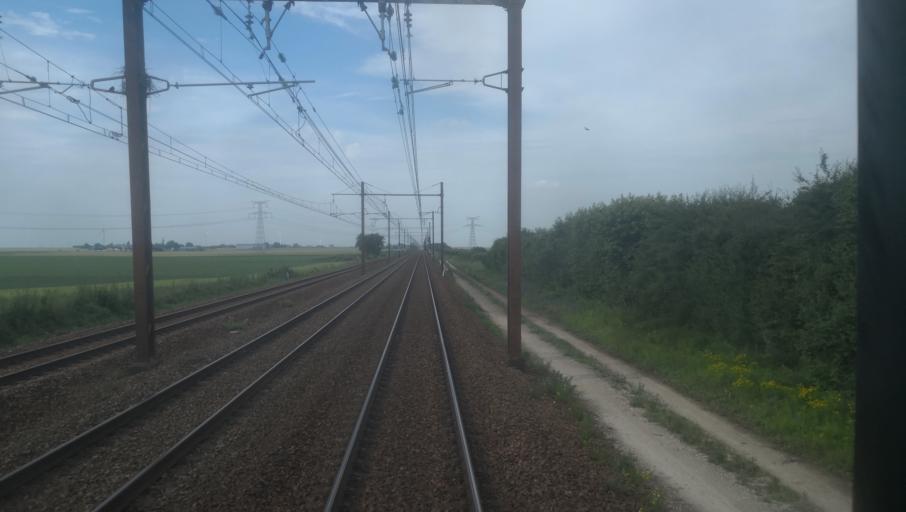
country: FR
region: Centre
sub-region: Departement du Loiret
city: Artenay
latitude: 48.1266
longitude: 1.9049
